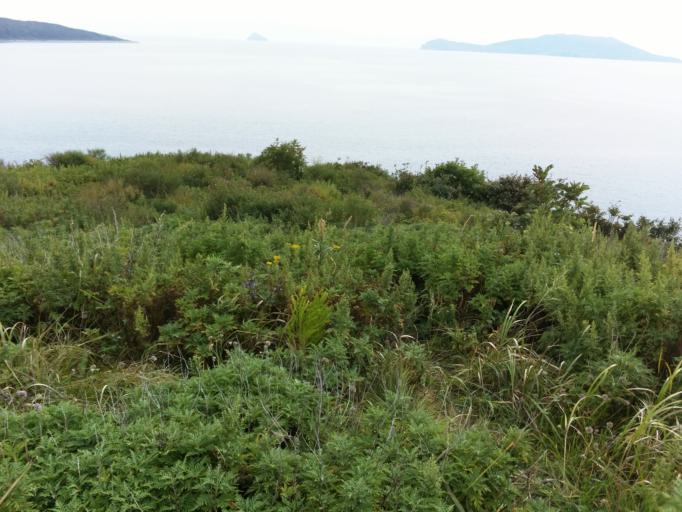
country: RU
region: Primorskiy
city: Popova
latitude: 42.9196
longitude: 131.7121
